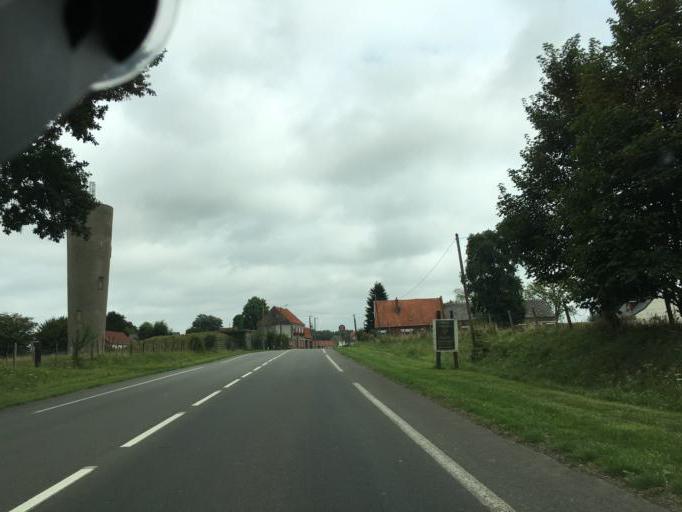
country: FR
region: Nord-Pas-de-Calais
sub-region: Departement du Pas-de-Calais
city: Saint-Pol-sur-Ternoise
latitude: 50.4106
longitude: 2.3760
